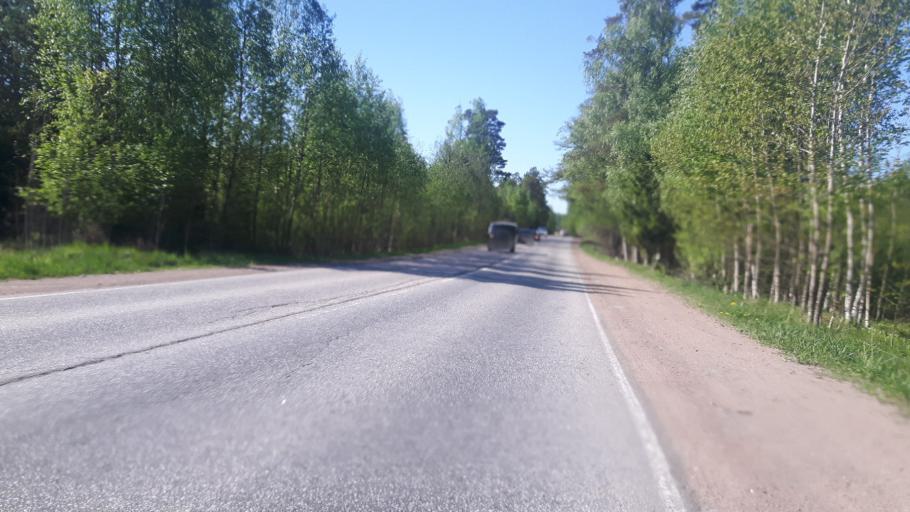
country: RU
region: Leningrad
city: Vyborg
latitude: 60.6467
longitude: 28.7473
